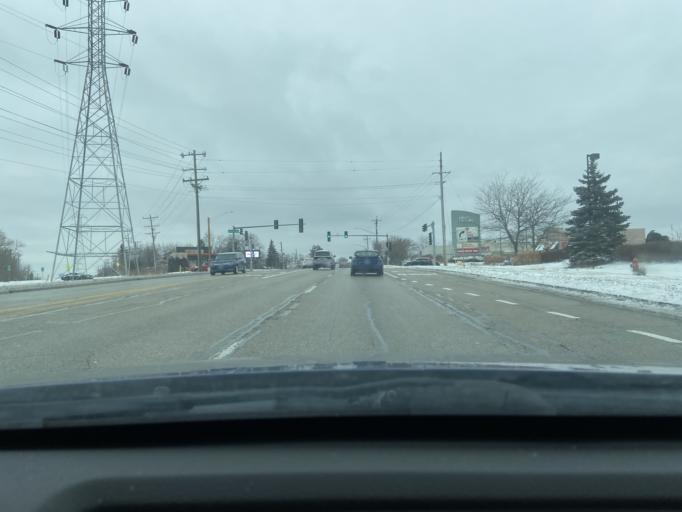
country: US
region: Illinois
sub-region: Lake County
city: Round Lake Beach
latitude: 42.3790
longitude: -88.0719
